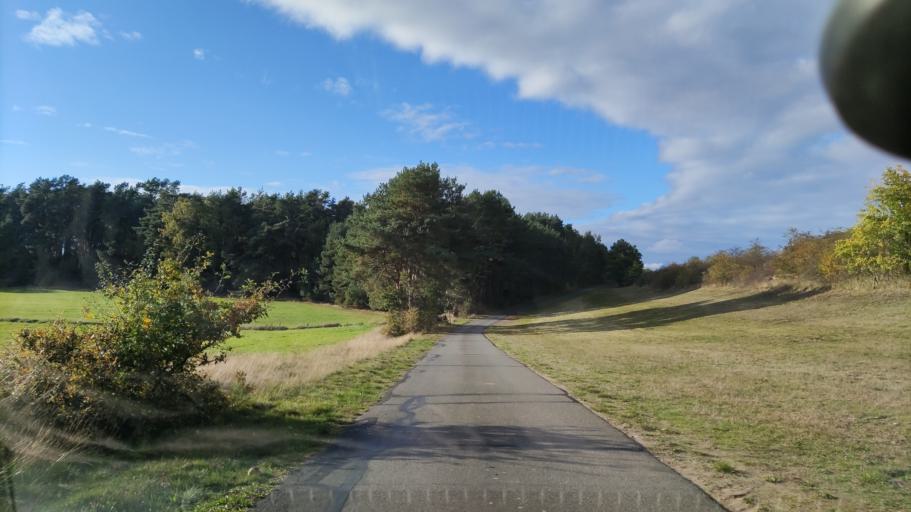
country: DE
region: Lower Saxony
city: Vastorf
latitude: 53.1671
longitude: 10.5273
